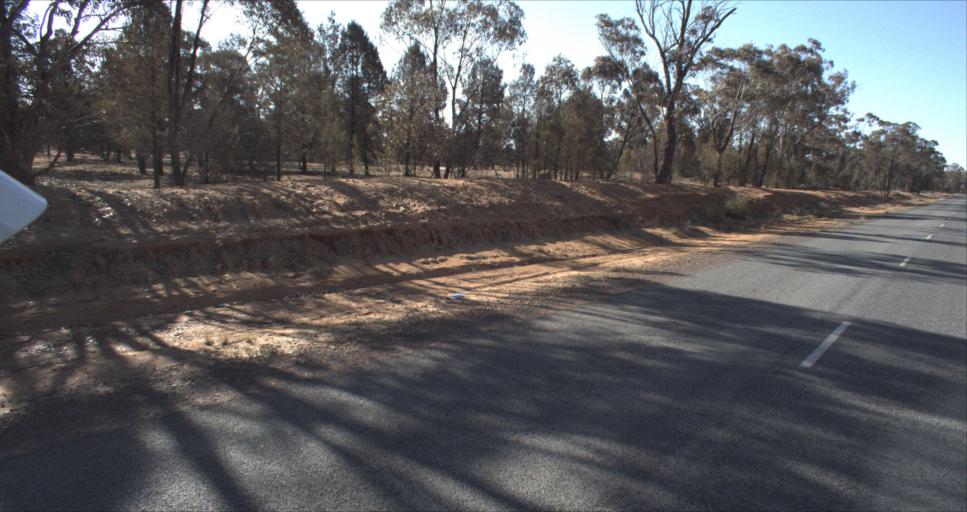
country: AU
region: New South Wales
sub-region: Leeton
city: Leeton
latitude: -34.6492
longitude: 146.3516
